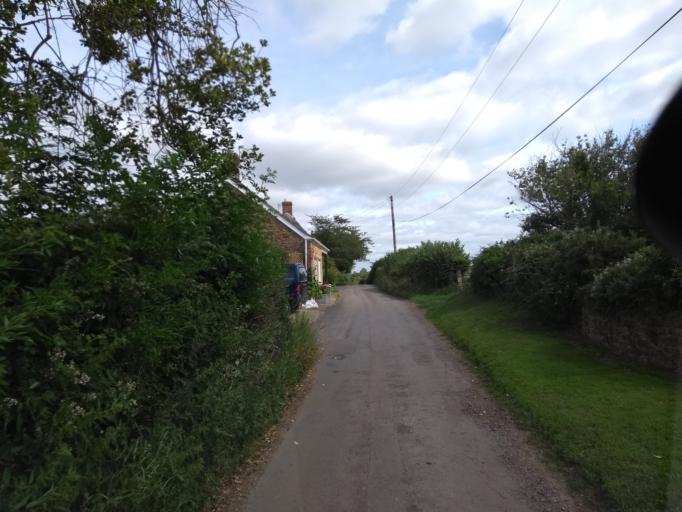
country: GB
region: England
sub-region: Somerset
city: Ilminster
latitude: 50.9173
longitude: -2.8653
